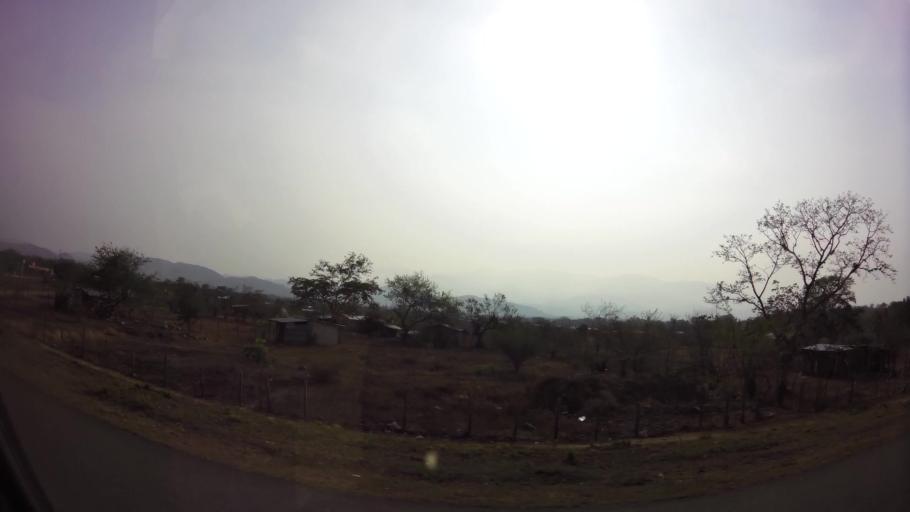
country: HN
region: Comayagua
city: Comayagua
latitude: 14.4561
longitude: -87.6656
